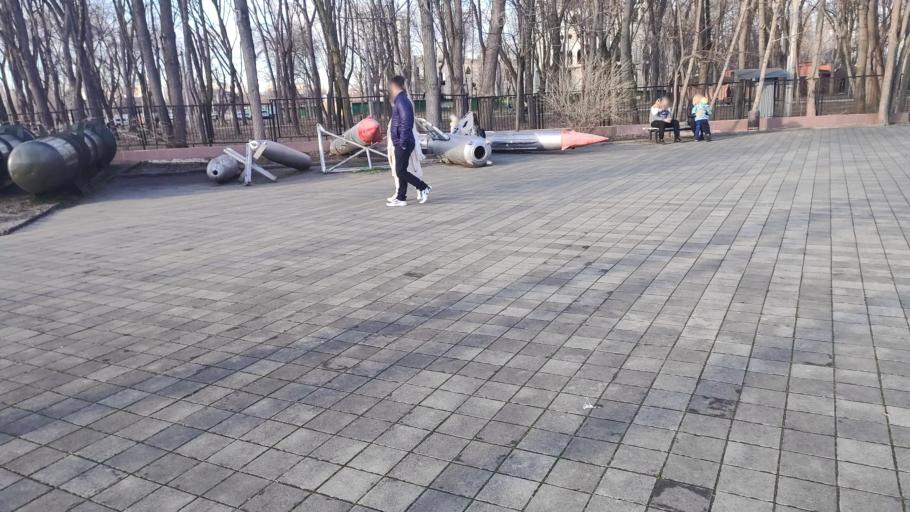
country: RU
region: Krasnodarskiy
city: Krasnodar
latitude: 45.0220
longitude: 38.9540
